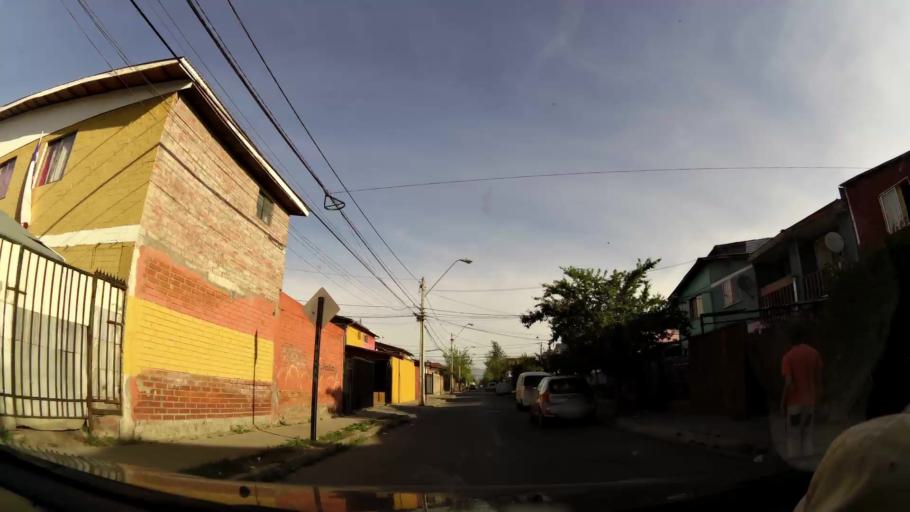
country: CL
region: Santiago Metropolitan
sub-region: Provincia de Cordillera
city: Puente Alto
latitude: -33.5942
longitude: -70.5694
